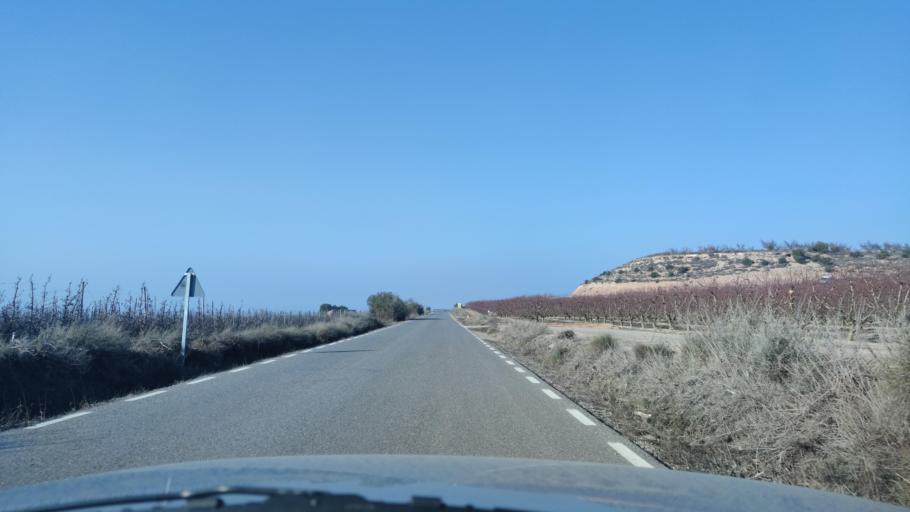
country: ES
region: Catalonia
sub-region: Provincia de Lleida
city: Sunyer
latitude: 41.5180
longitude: 0.5655
